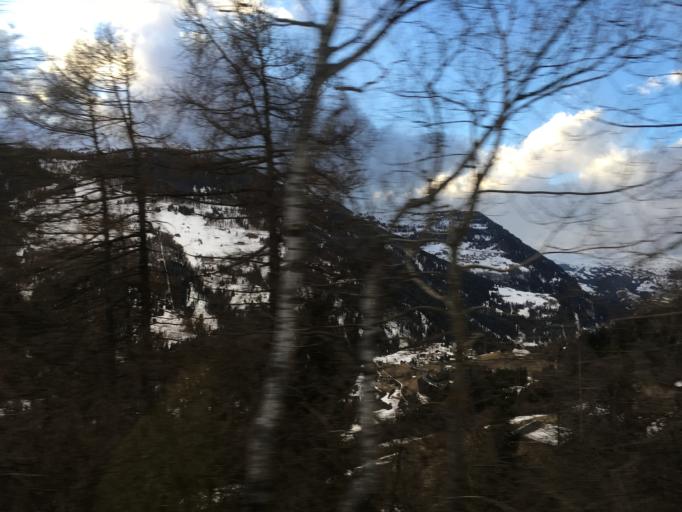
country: CH
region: Grisons
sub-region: Albula District
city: Tiefencastel
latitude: 46.6742
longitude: 9.5707
